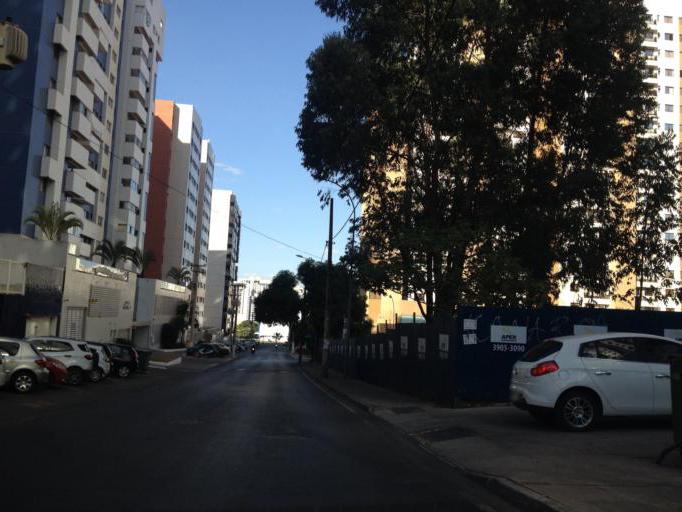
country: BR
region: Federal District
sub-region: Brasilia
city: Brasilia
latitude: -15.8371
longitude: -48.0294
